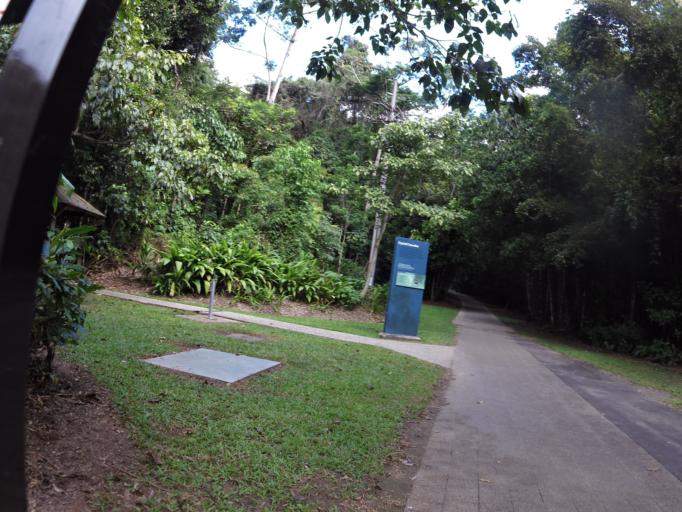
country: AU
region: Queensland
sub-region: Cairns
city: Woree
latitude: -16.9622
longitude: 145.6794
